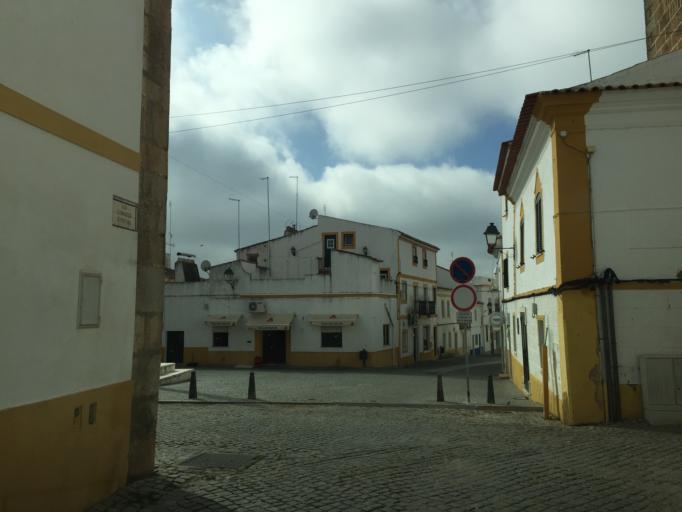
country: PT
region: Portalegre
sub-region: Fronteira
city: Fronteira
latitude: 39.0569
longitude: -7.6475
